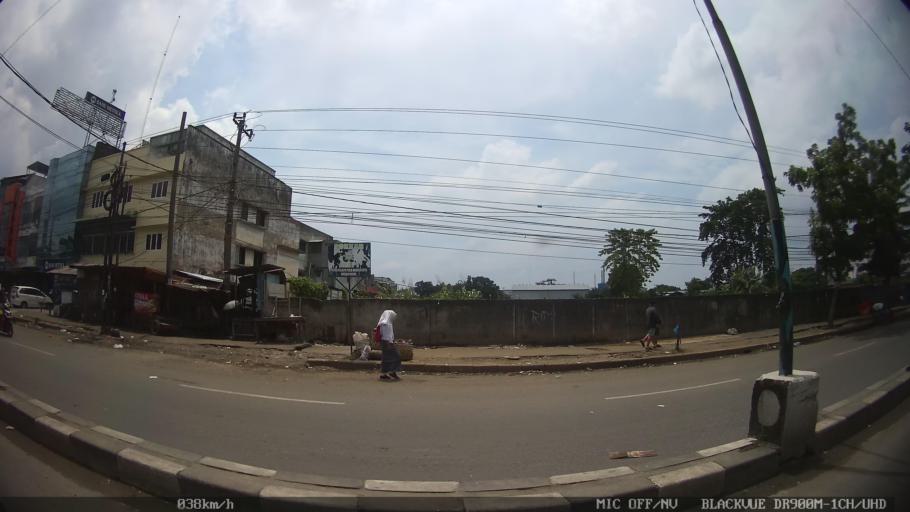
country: ID
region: North Sumatra
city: Medan
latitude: 3.6320
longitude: 98.6695
